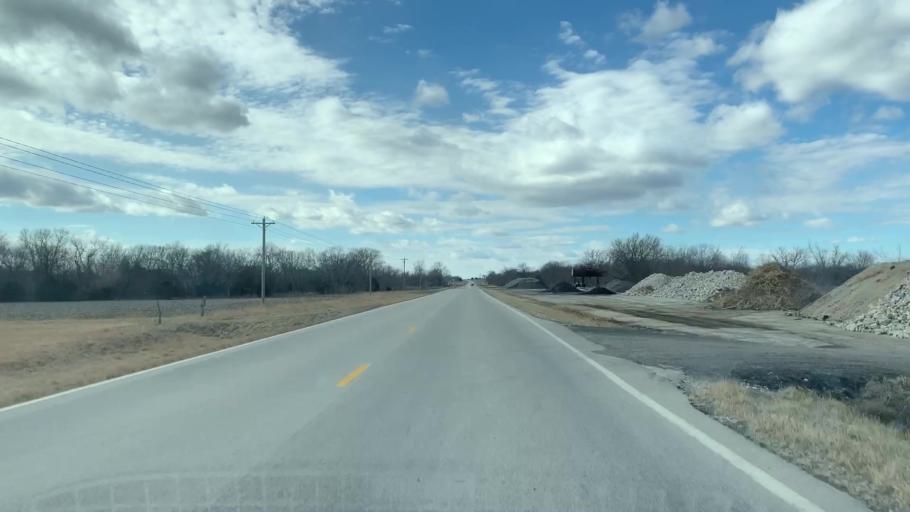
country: US
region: Kansas
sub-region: Neosho County
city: Erie
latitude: 37.5293
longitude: -95.2860
